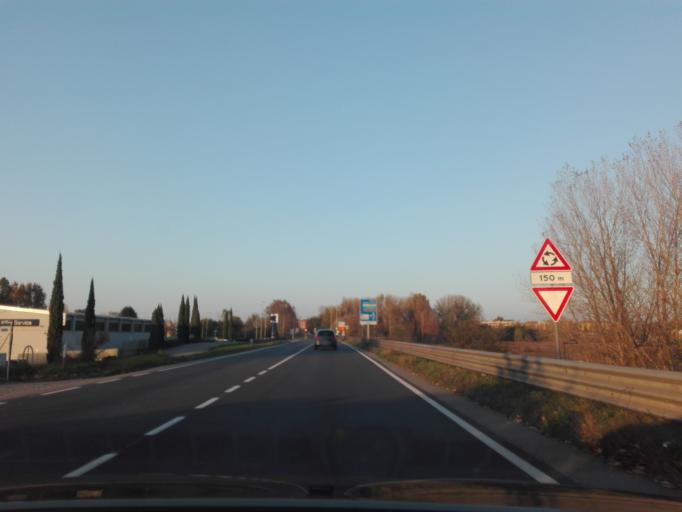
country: IT
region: Lombardy
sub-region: Provincia di Mantova
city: Cerese
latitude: 45.1378
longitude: 10.7936
